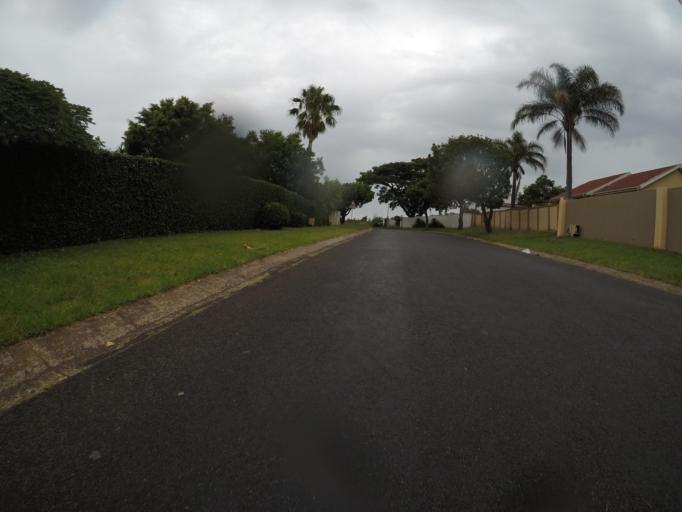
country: ZA
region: Eastern Cape
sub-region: Buffalo City Metropolitan Municipality
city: East London
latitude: -32.9897
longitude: 27.8490
